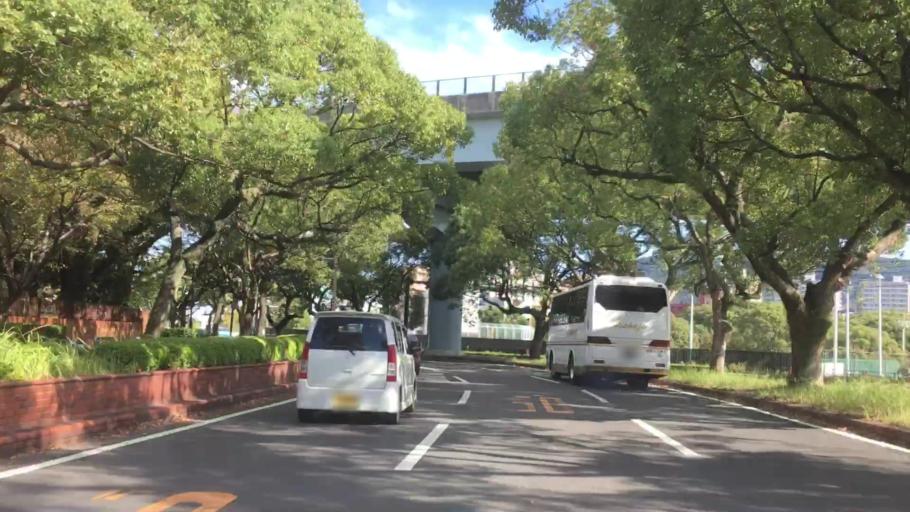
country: JP
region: Nagasaki
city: Sasebo
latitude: 33.1693
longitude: 129.7143
